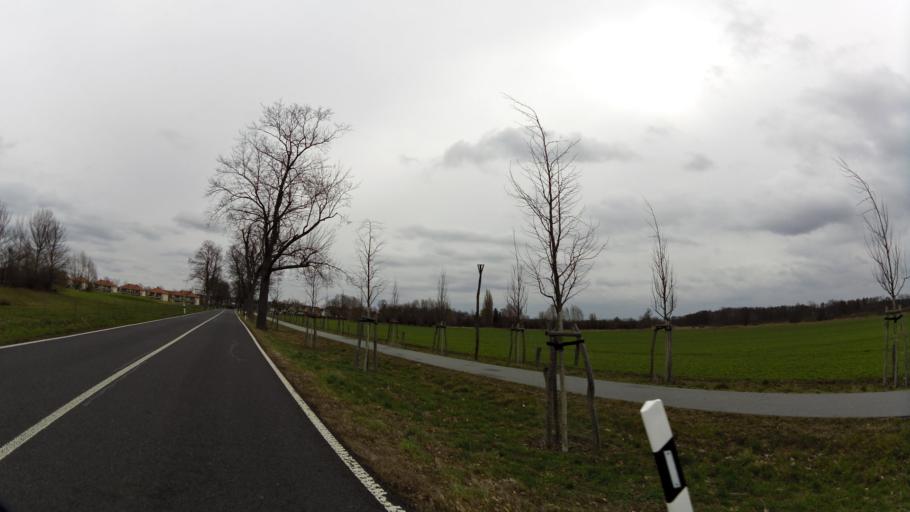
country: DE
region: Brandenburg
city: Rangsdorf
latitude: 52.3272
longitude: 13.4558
